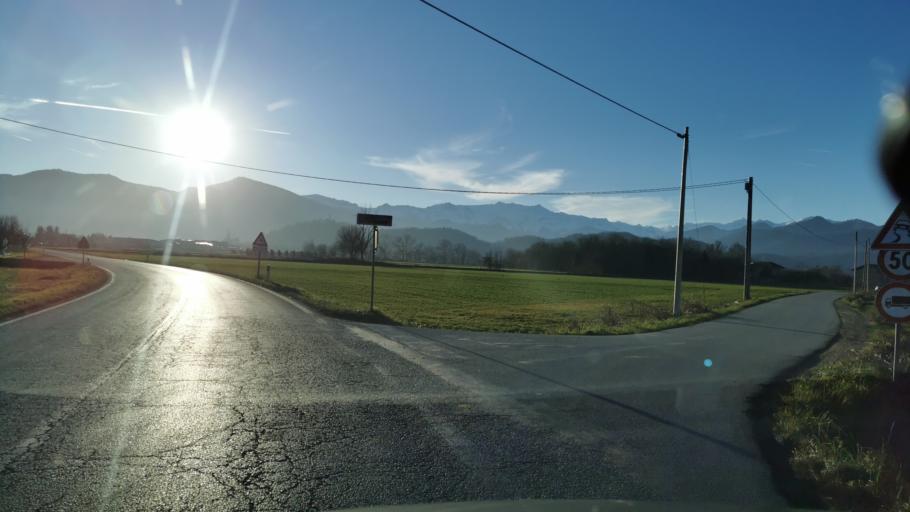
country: IT
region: Piedmont
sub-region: Provincia di Cuneo
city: Caraglio
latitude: 44.4309
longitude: 7.4482
